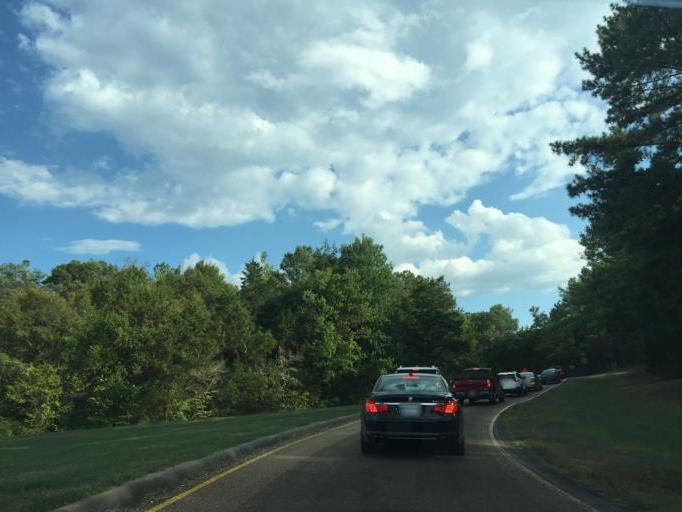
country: US
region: Mississippi
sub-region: Madison County
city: Ridgeland
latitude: 32.4270
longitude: -90.1089
